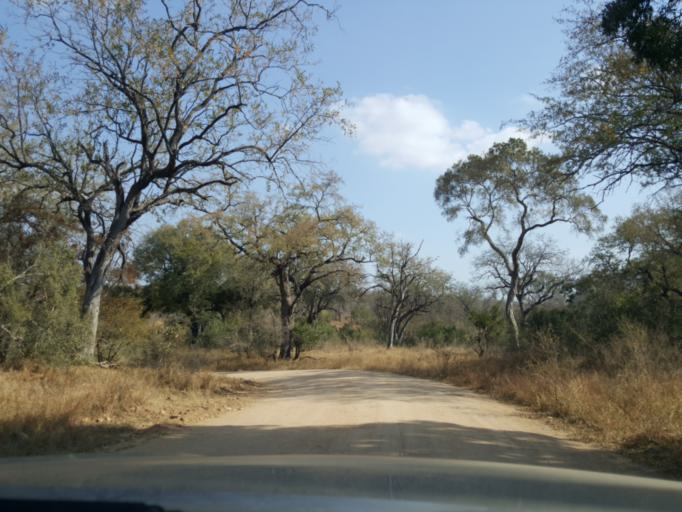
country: ZA
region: Mpumalanga
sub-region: Ehlanzeni District
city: Komatipoort
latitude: -25.2907
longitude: 31.7641
